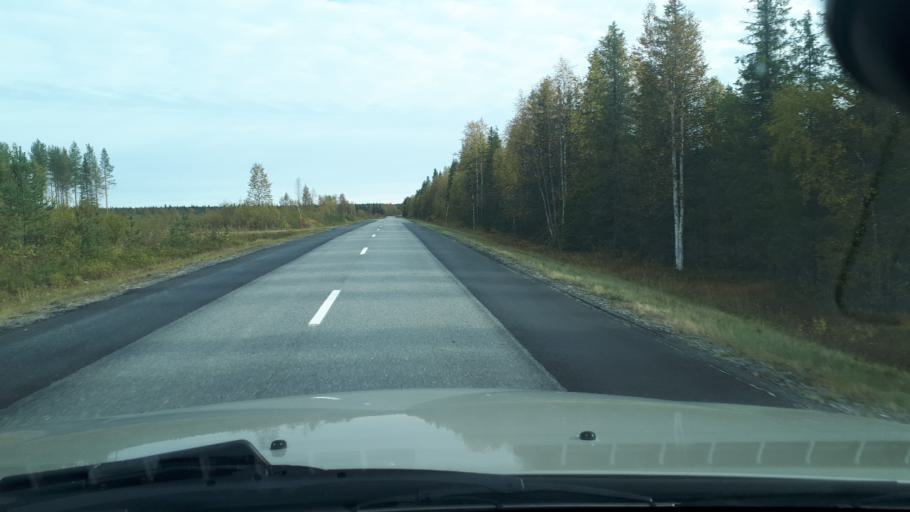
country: FI
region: Lapland
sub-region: Rovaniemi
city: Ranua
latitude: 65.9810
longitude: 26.1395
